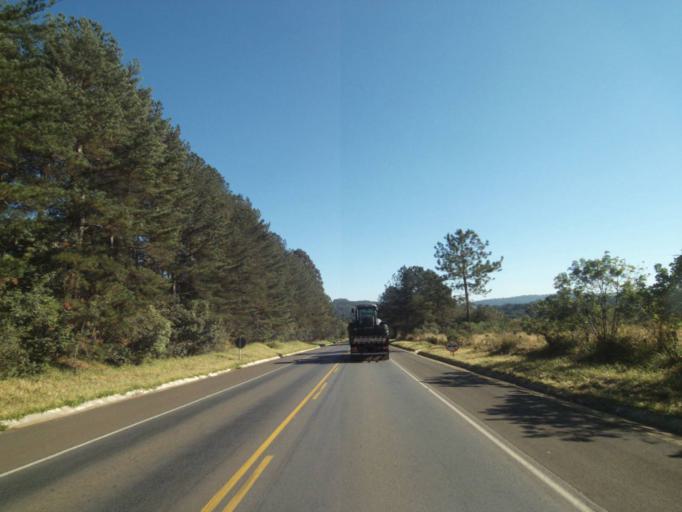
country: BR
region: Parana
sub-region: Tibagi
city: Tibagi
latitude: -24.4844
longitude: -50.4402
